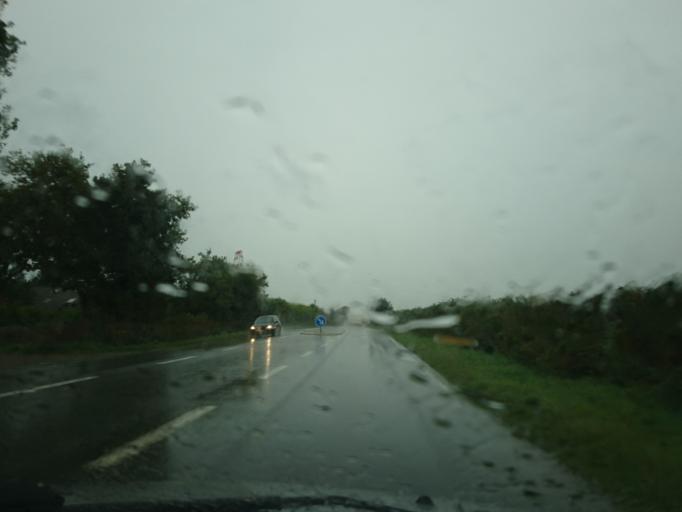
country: FR
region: Brittany
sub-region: Departement du Finistere
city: Plabennec
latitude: 48.4801
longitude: -4.4371
